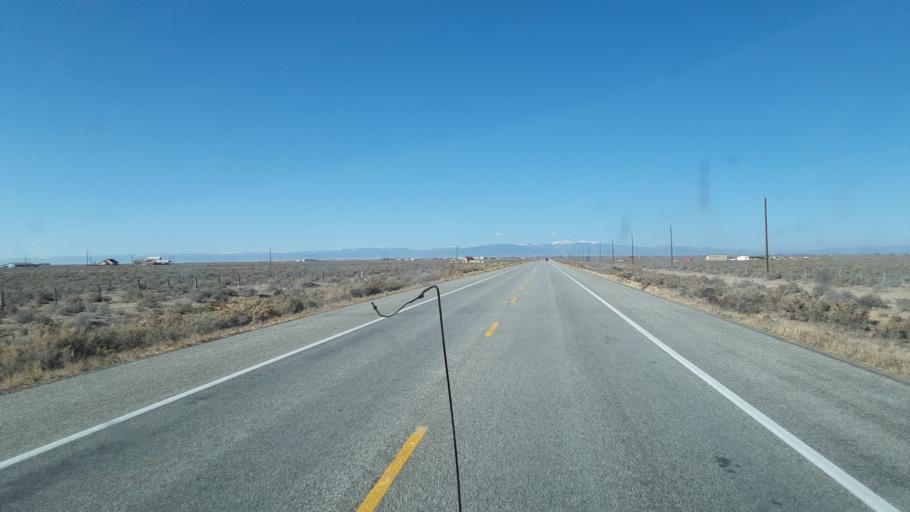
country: US
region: Colorado
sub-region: Alamosa County
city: Alamosa East
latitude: 37.4747
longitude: -105.6710
